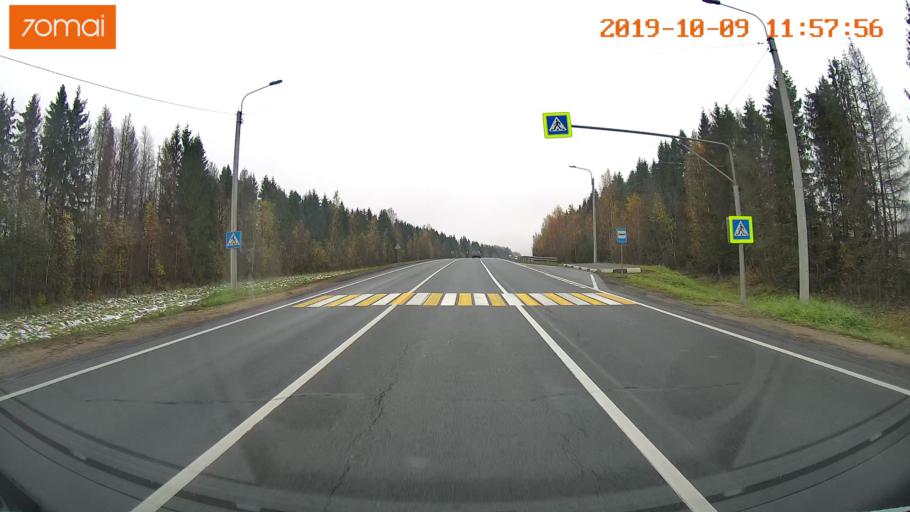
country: RU
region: Vologda
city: Gryazovets
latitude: 58.7253
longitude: 40.2954
